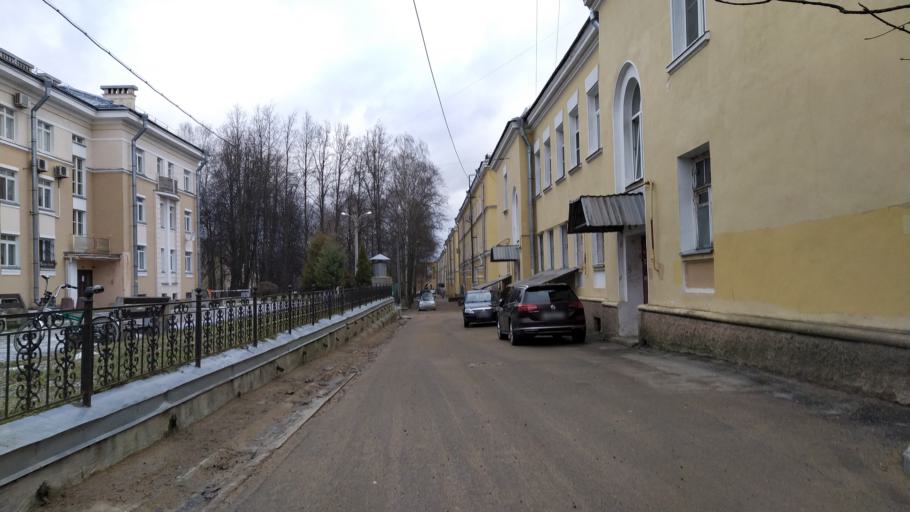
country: RU
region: St.-Petersburg
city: Pushkin
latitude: 59.7224
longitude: 30.4217
